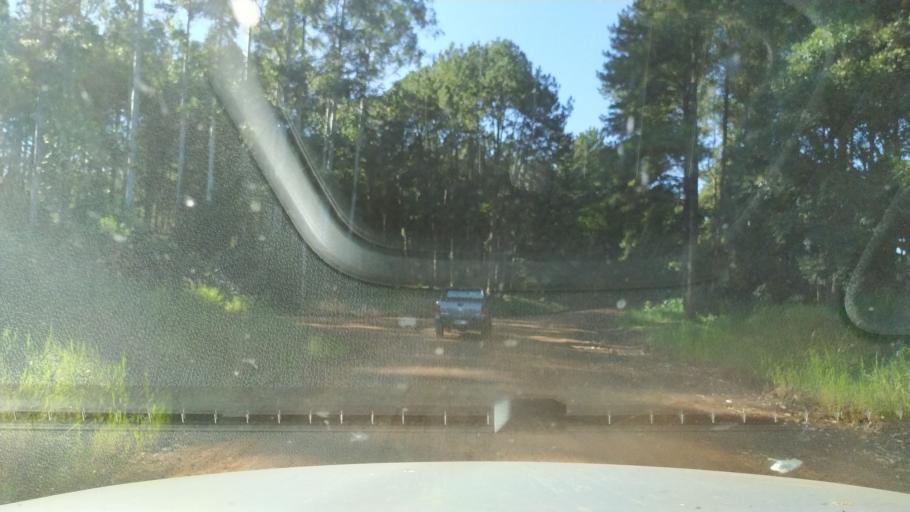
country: AR
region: Misiones
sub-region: Departamento de Montecarlo
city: Montecarlo
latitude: -26.6084
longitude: -54.6988
